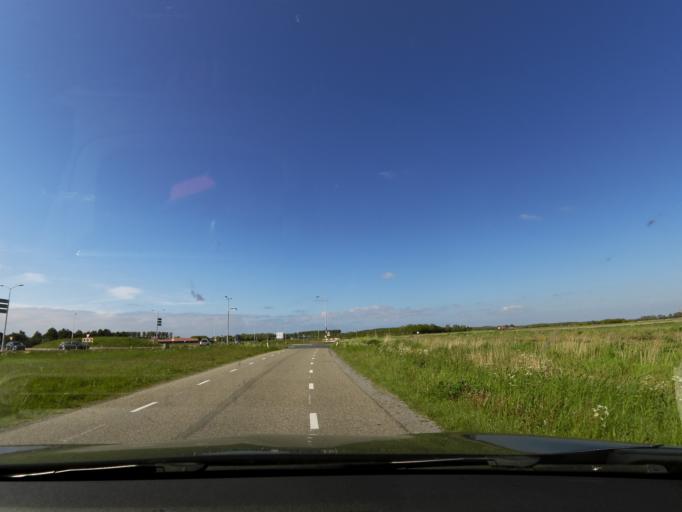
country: NL
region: South Holland
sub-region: Gemeente Goeree-Overflakkee
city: Ouddorp
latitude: 51.8075
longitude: 3.9451
